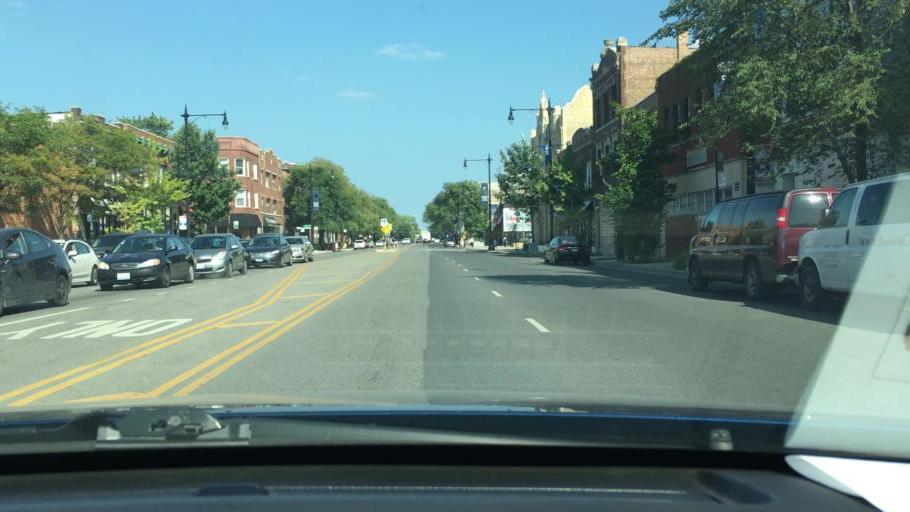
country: US
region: Illinois
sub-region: Cook County
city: Lincolnwood
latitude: 41.9247
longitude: -87.7116
